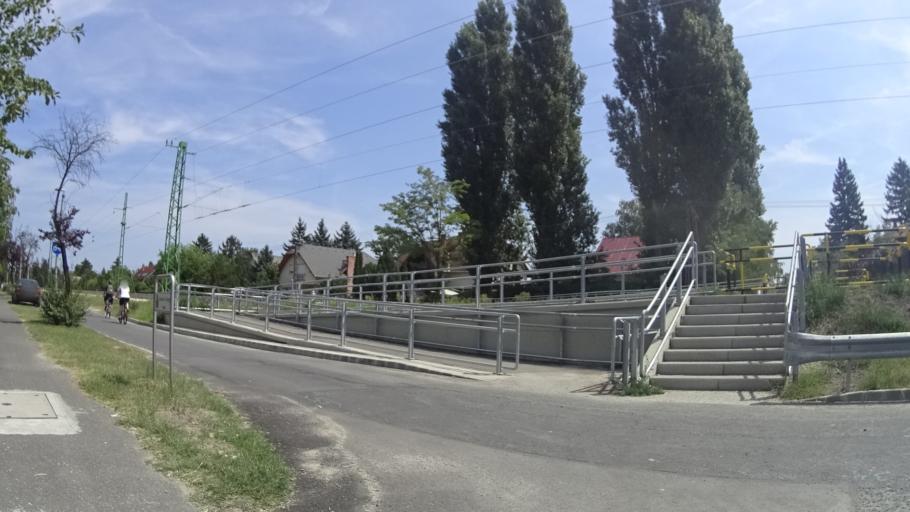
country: HU
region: Somogy
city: Fonyod
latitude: 46.7549
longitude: 17.5775
